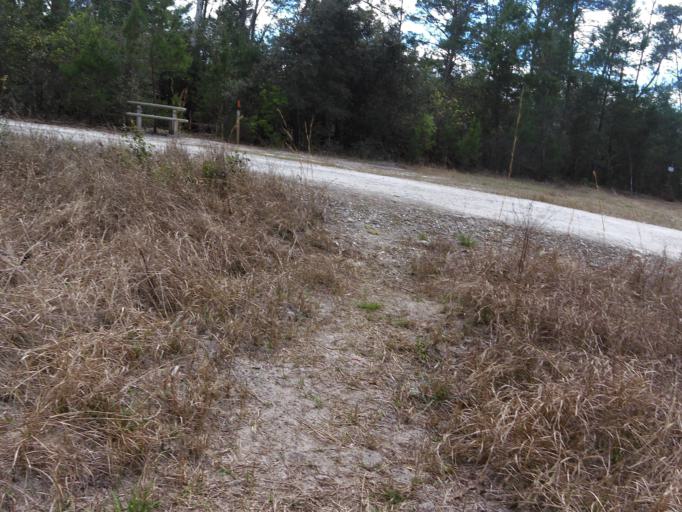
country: US
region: Florida
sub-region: Putnam County
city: Interlachen
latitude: 29.7657
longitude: -81.8655
